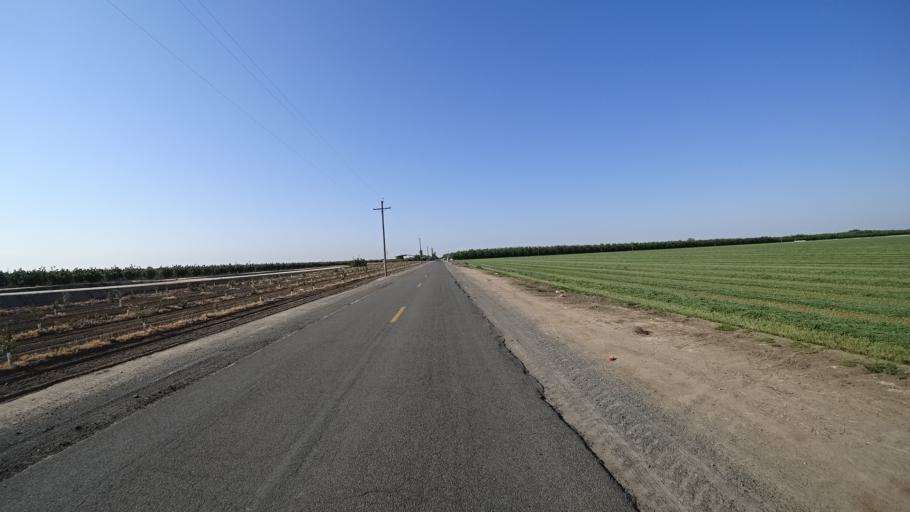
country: US
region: California
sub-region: Kings County
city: Home Garden
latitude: 36.2798
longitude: -119.5652
